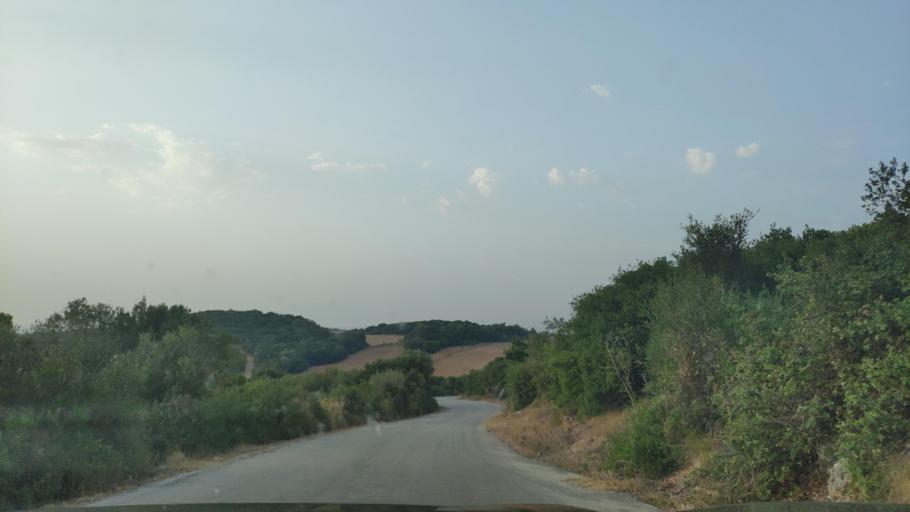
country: GR
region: West Greece
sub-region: Nomos Aitolias kai Akarnanias
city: Monastirakion
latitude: 38.9209
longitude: 20.9802
